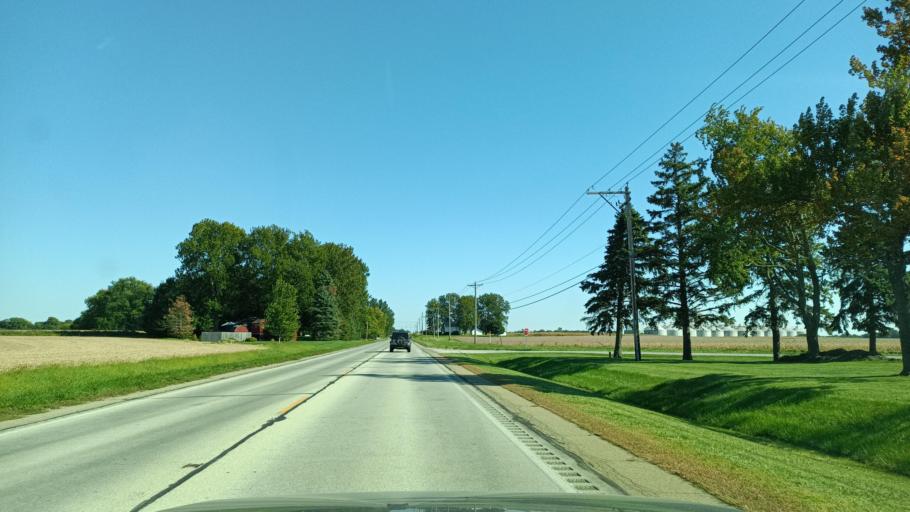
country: US
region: Illinois
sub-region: Champaign County
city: Lake of the Woods
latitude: 40.1682
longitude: -88.3314
